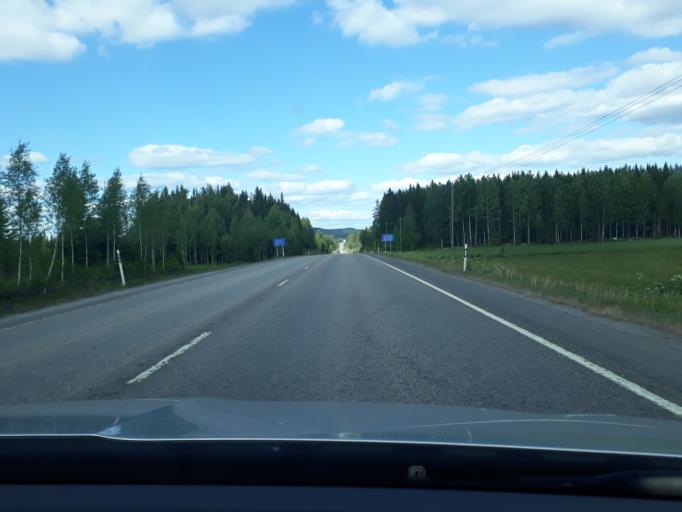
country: FI
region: Central Finland
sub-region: AEaenekoski
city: AEaenekoski
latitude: 62.6486
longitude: 25.7134
